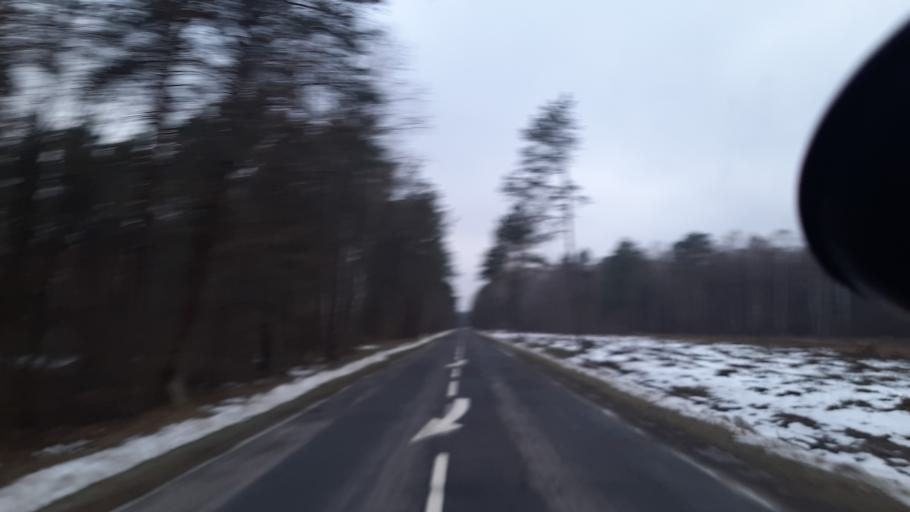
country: PL
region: Lublin Voivodeship
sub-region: Powiat parczewski
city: Podedworze
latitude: 51.5696
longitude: 23.2503
